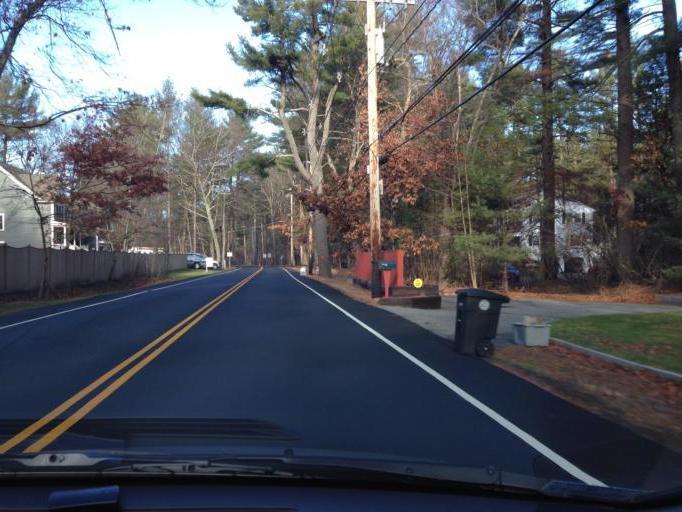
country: US
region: Massachusetts
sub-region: Middlesex County
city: Bedford
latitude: 42.5040
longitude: -71.3012
